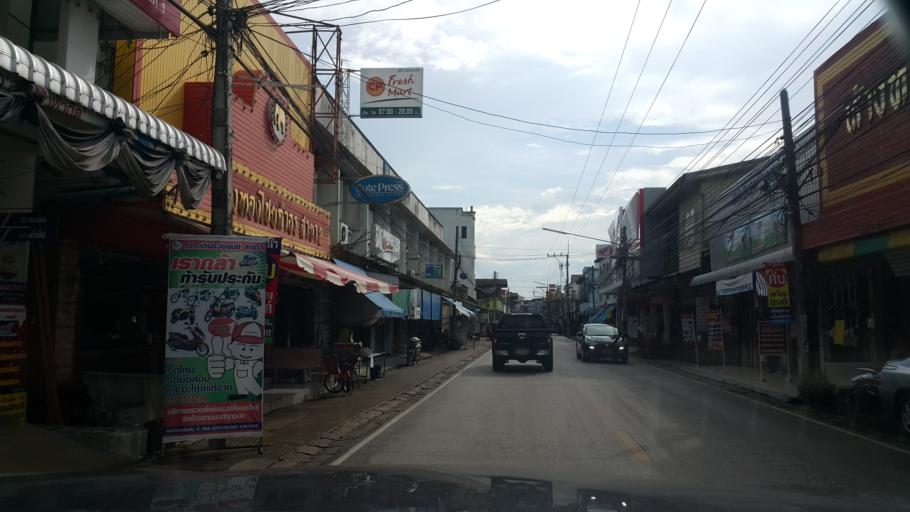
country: TH
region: Lampang
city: Thoen
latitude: 17.6065
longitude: 99.2110
